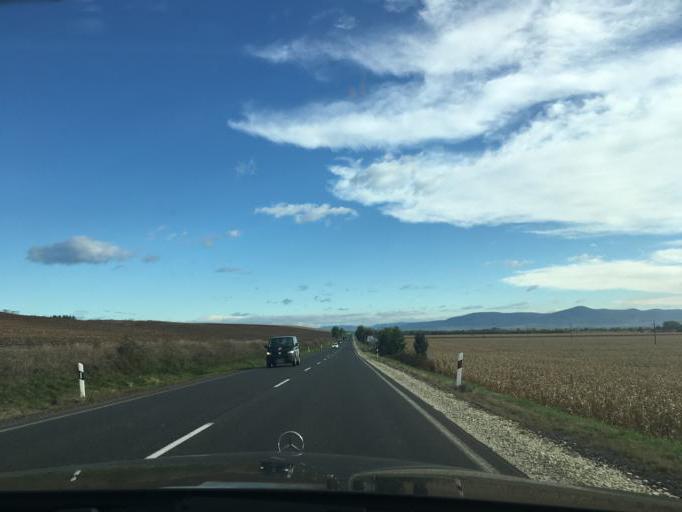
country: HU
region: Borsod-Abauj-Zemplen
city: Encs
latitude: 48.3419
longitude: 21.1148
